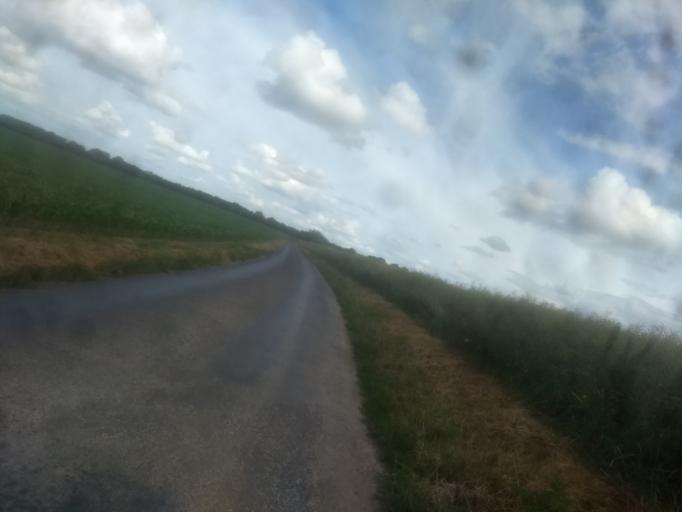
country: FR
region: Nord-Pas-de-Calais
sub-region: Departement du Pas-de-Calais
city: Duisans
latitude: 50.2910
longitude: 2.6943
